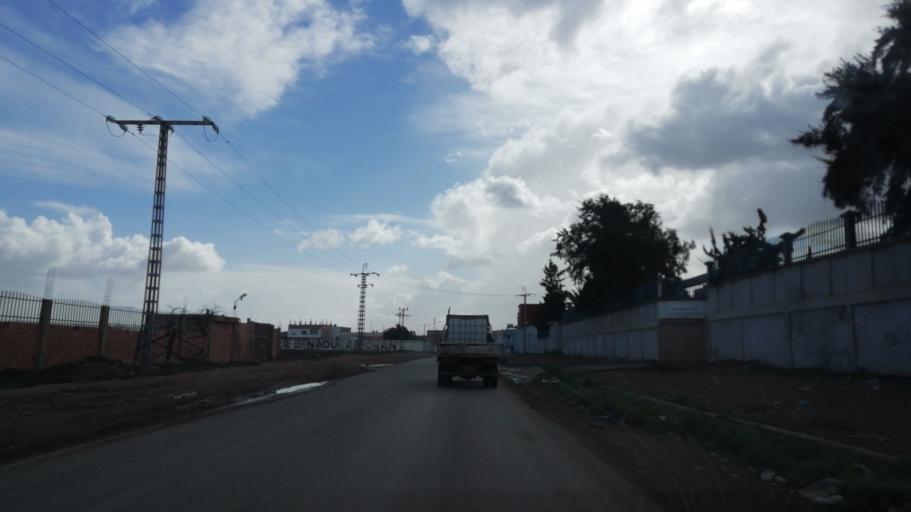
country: DZ
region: Oran
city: Sidi ech Chahmi
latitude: 35.6416
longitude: -0.5536
